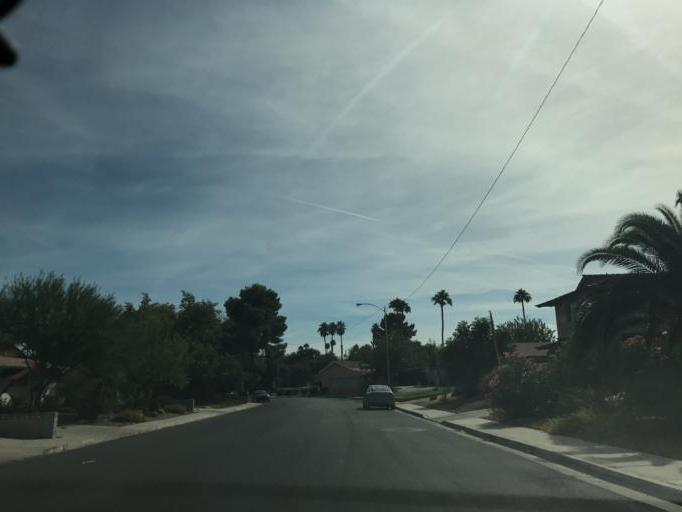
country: US
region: Nevada
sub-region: Clark County
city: Winchester
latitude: 36.1287
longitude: -115.1000
